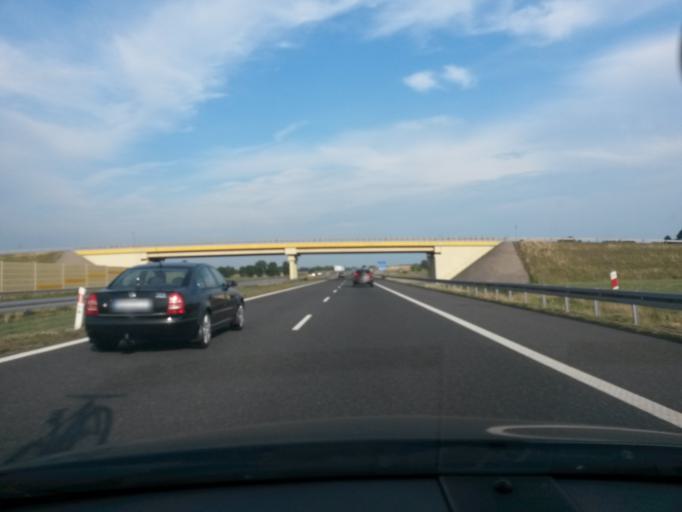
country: PL
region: Lodz Voivodeship
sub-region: Powiat poddebicki
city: Dalikow
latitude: 51.9672
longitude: 19.1046
